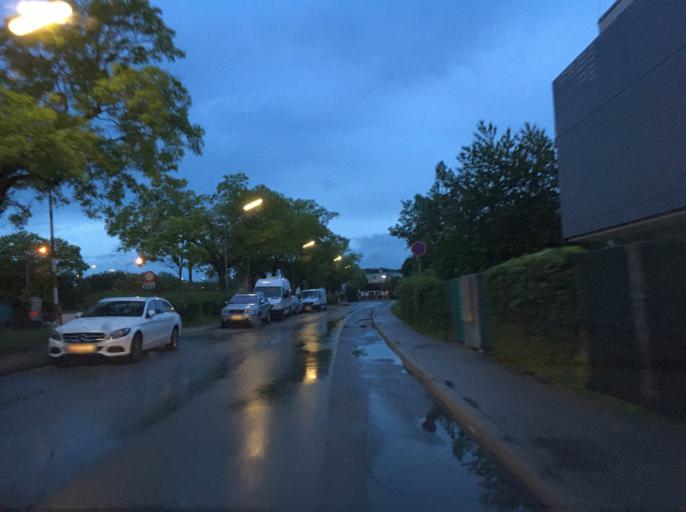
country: AT
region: Vienna
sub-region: Wien Stadt
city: Vienna
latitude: 48.2413
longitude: 16.4048
